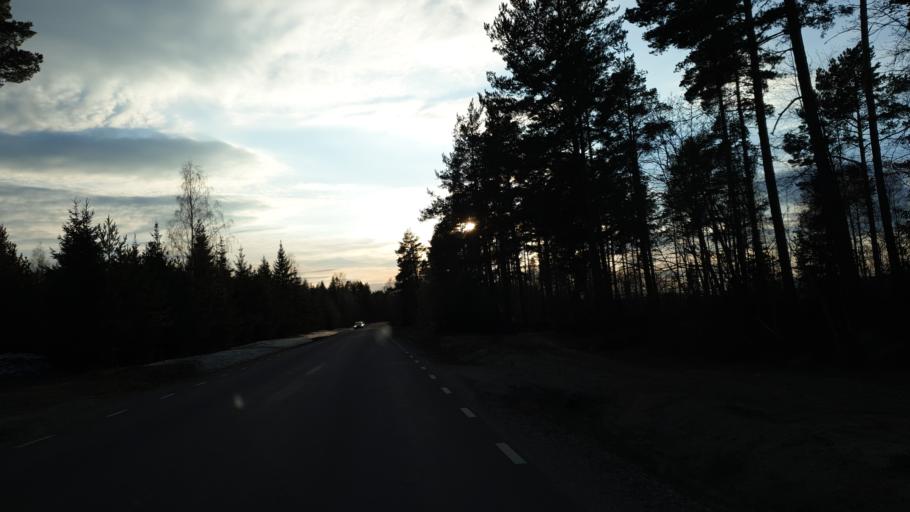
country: SE
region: Vaesternorrland
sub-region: Sundsvalls Kommun
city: Njurundabommen
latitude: 62.2656
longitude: 17.4267
